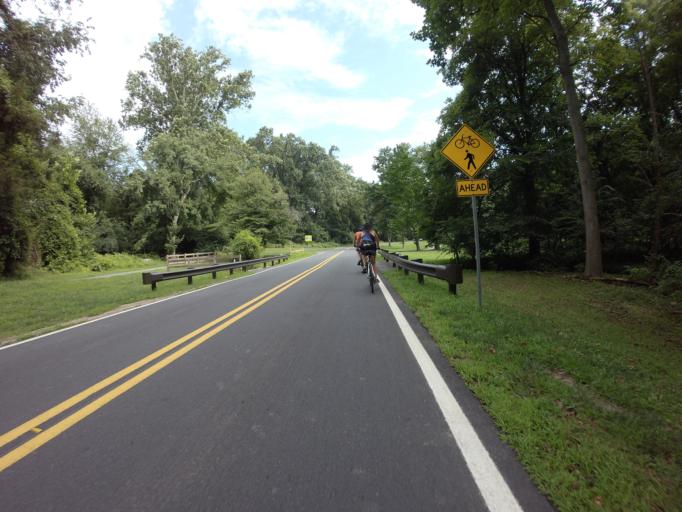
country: US
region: Maryland
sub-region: Montgomery County
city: Forest Glen
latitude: 39.0114
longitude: -77.0680
